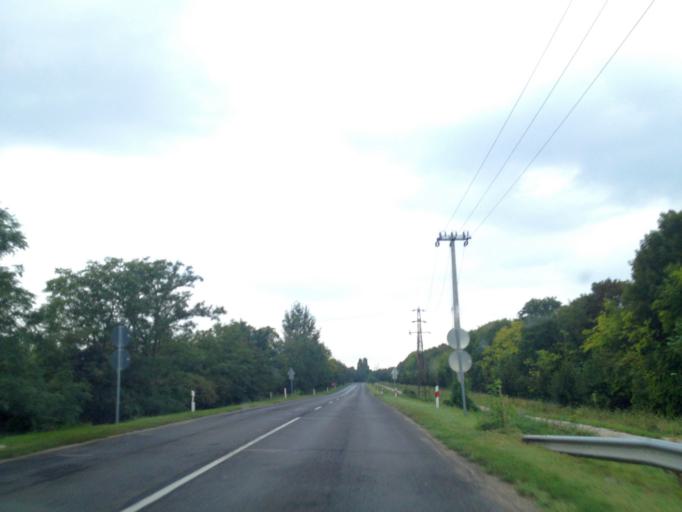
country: AT
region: Burgenland
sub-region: Politischer Bezirk Neusiedl am See
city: Nickelsdorf
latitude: 47.9192
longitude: 17.1393
